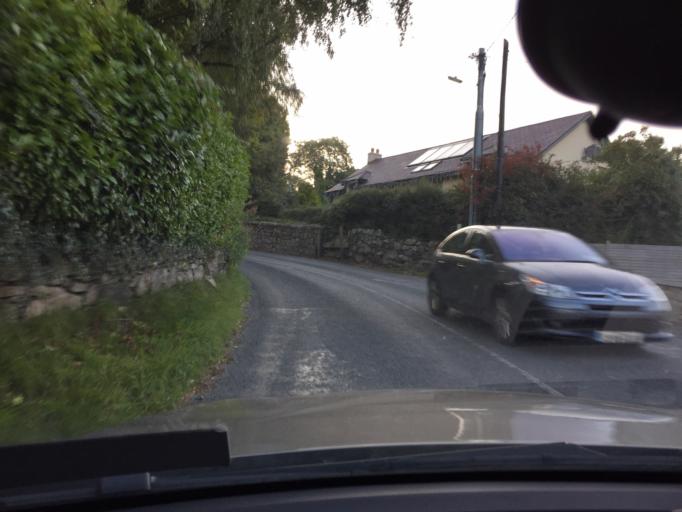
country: IE
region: Leinster
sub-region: Wicklow
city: Enniskerry
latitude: 53.1963
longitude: -6.1930
